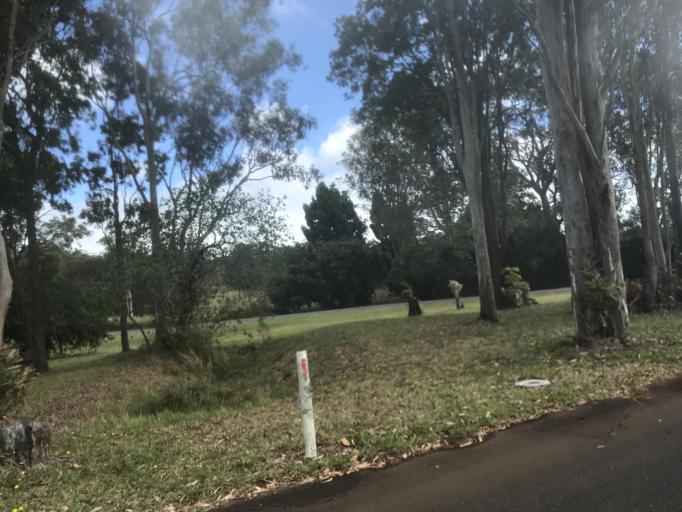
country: AU
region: Queensland
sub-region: Tablelands
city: Tolga
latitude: -17.2176
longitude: 145.4654
